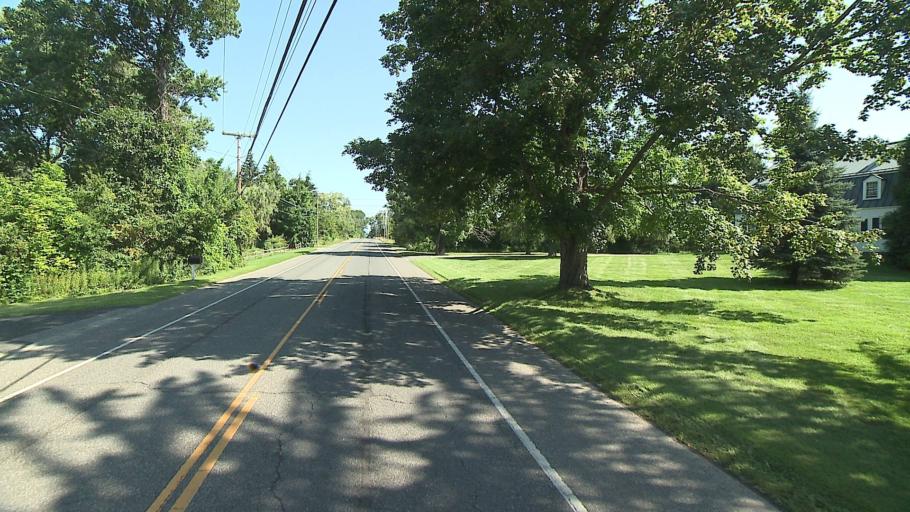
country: US
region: Connecticut
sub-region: Litchfield County
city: Canaan
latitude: 41.9005
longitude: -73.4481
